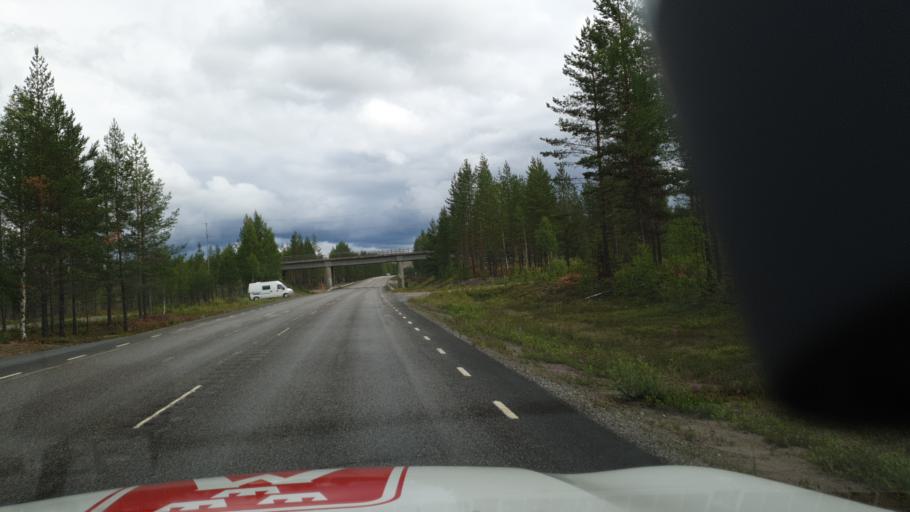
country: SE
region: Vaesterbotten
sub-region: Skelleftea Kommun
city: Langsele
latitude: 64.9305
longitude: 19.9935
